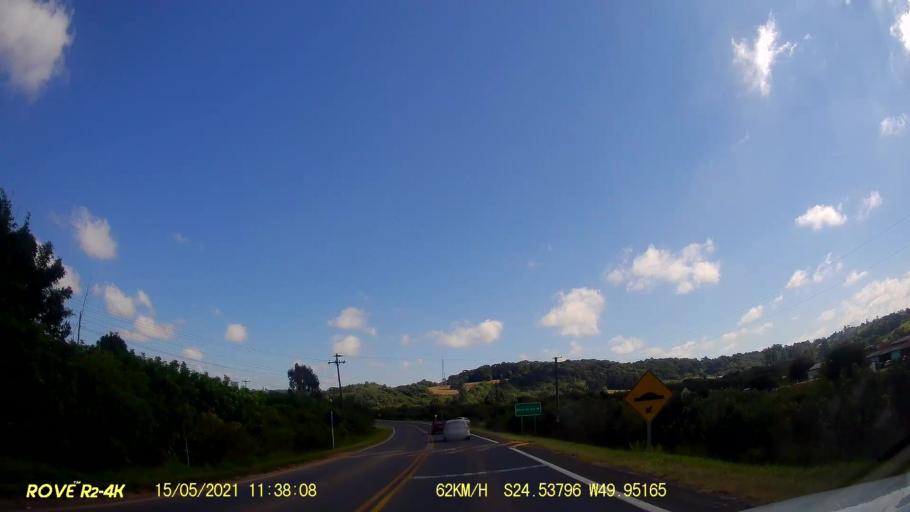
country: BR
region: Parana
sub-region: Pirai Do Sul
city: Pirai do Sul
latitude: -24.5376
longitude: -49.9500
